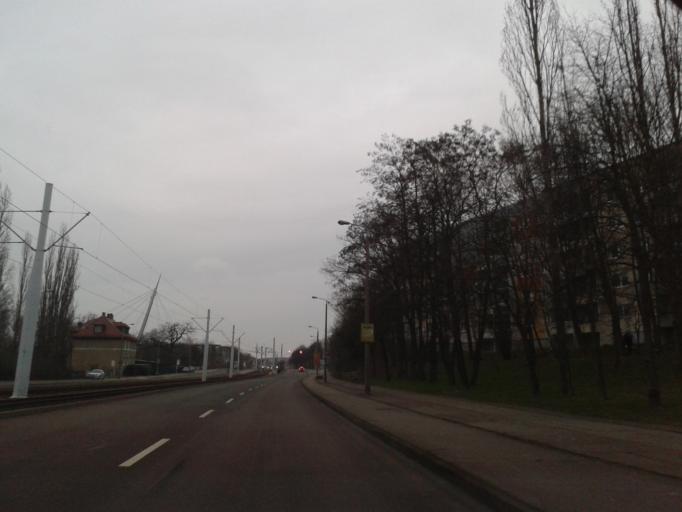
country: DE
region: Saxony-Anhalt
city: Halle Neustadt
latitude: 51.4573
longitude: 11.9452
